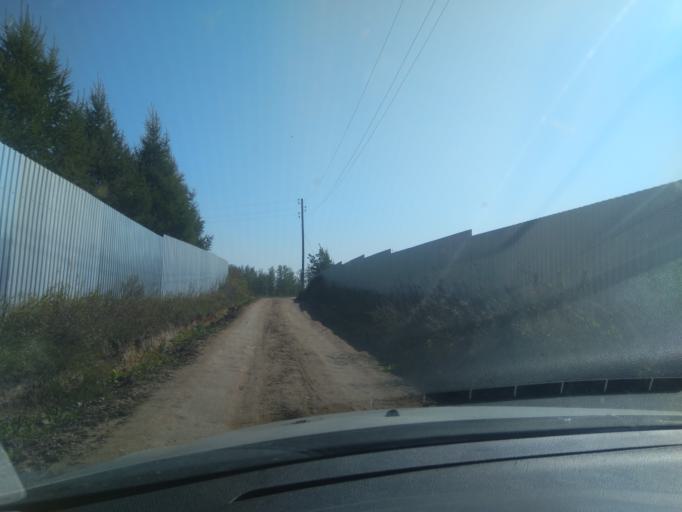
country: RU
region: Sverdlovsk
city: Pokrovskoye
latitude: 56.4363
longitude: 61.6009
